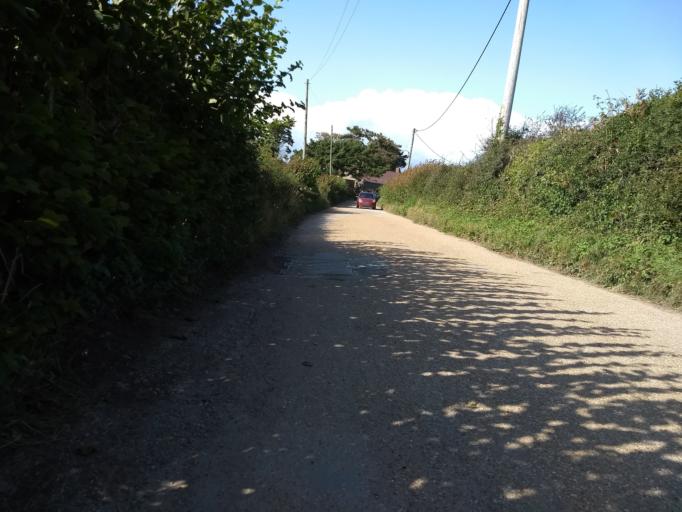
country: GB
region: England
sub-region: Isle of Wight
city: Totland
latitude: 50.6931
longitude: -1.5274
